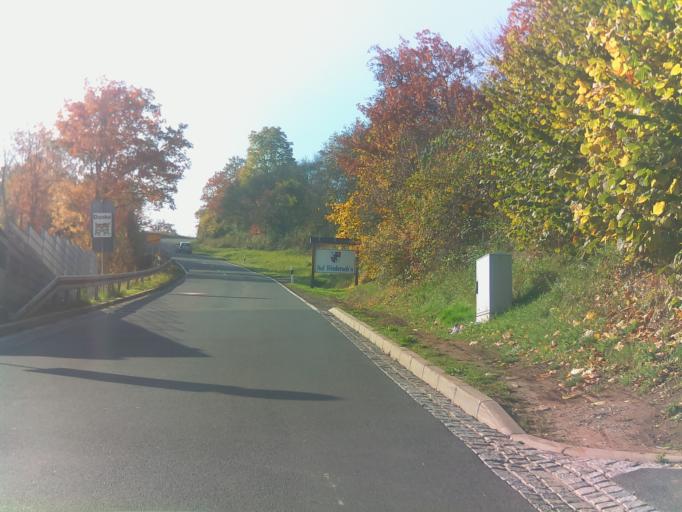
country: DE
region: Bavaria
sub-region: Regierungsbezirk Unterfranken
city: Eltmann
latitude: 49.9696
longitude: 10.6629
